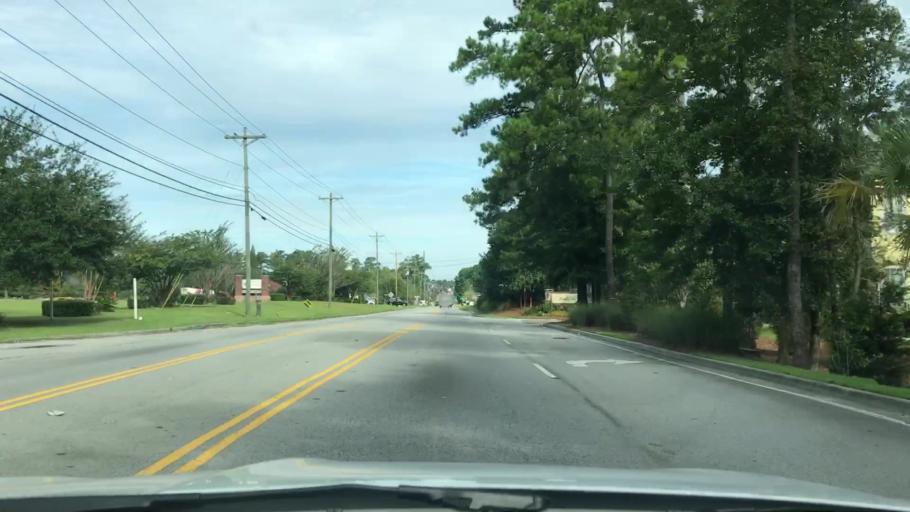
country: US
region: South Carolina
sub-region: Charleston County
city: Lincolnville
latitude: 33.0199
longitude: -80.1590
